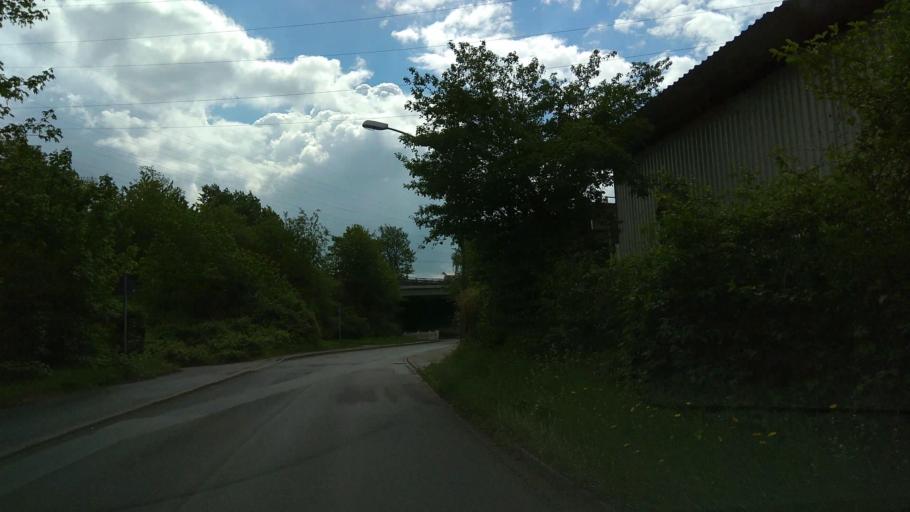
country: DE
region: North Rhine-Westphalia
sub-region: Regierungsbezirk Munster
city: Gelsenkirchen
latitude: 51.5267
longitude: 7.0736
